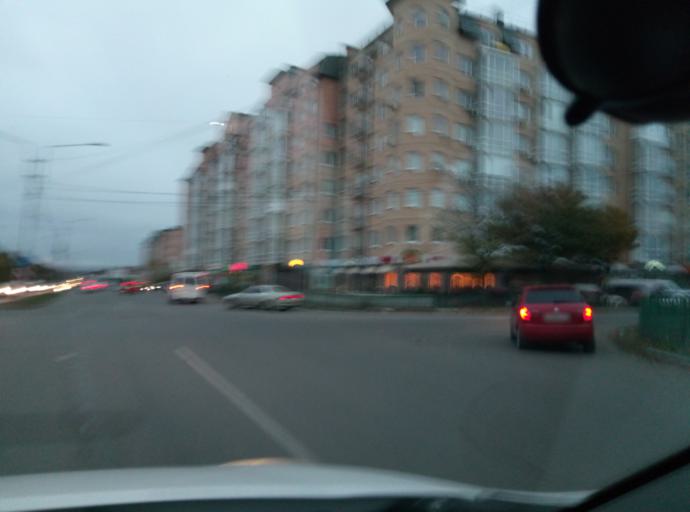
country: RU
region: Stavropol'skiy
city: Yessentukskaya
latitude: 44.0497
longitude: 42.8947
